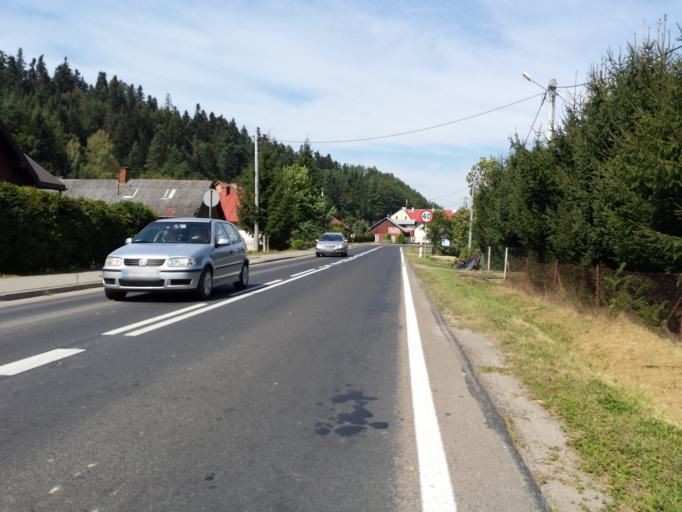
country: PL
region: Subcarpathian Voivodeship
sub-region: Powiat leski
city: Lesko
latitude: 49.4663
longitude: 22.3213
